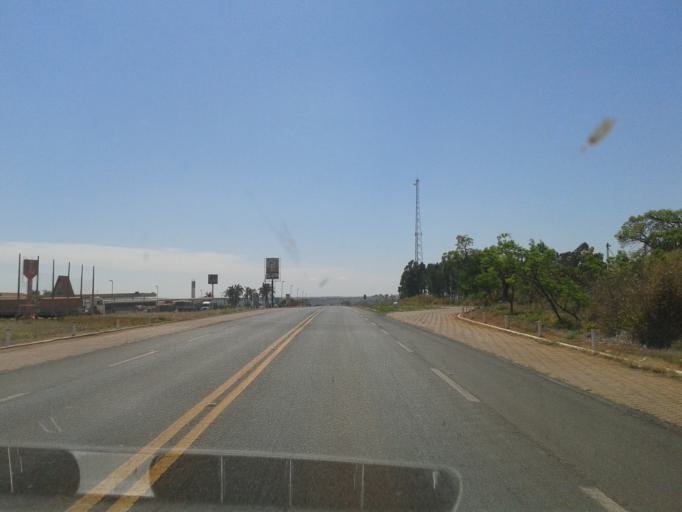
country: BR
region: Minas Gerais
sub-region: Sacramento
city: Sacramento
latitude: -19.3184
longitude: -47.5493
